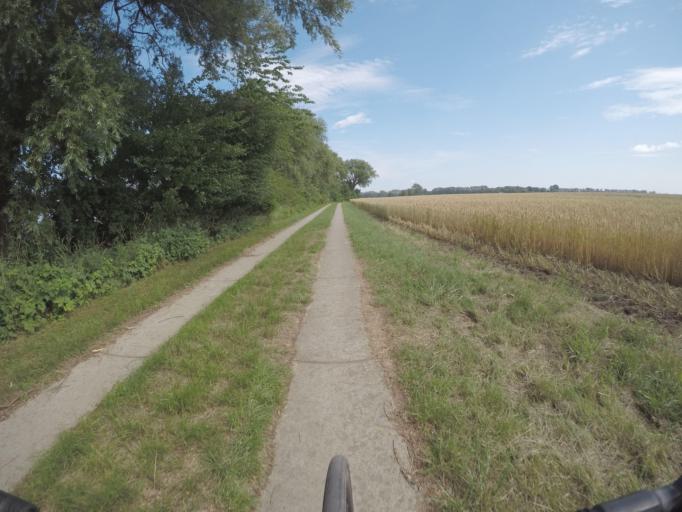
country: DE
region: Mecklenburg-Vorpommern
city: Altefahr
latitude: 54.3693
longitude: 13.1322
